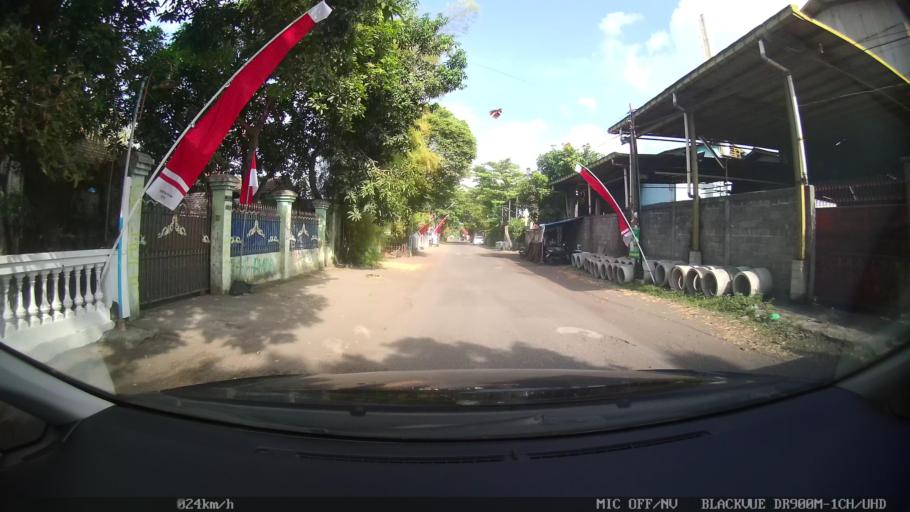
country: ID
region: Daerah Istimewa Yogyakarta
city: Kasihan
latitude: -7.8280
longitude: 110.3595
